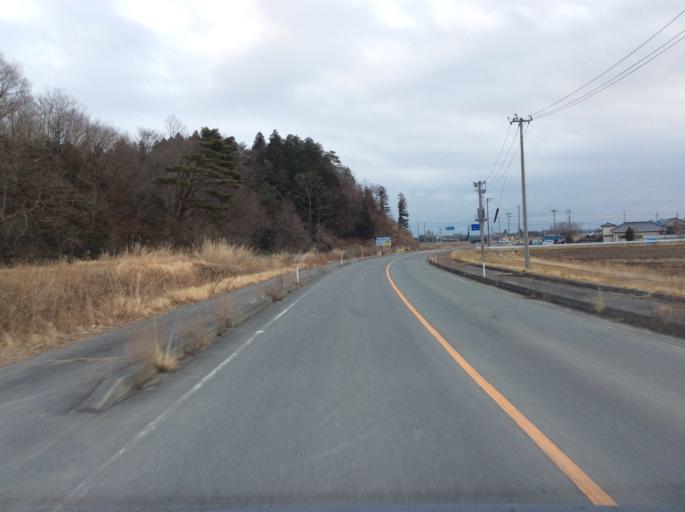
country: JP
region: Fukushima
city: Iwaki
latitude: 37.1172
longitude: 140.9555
